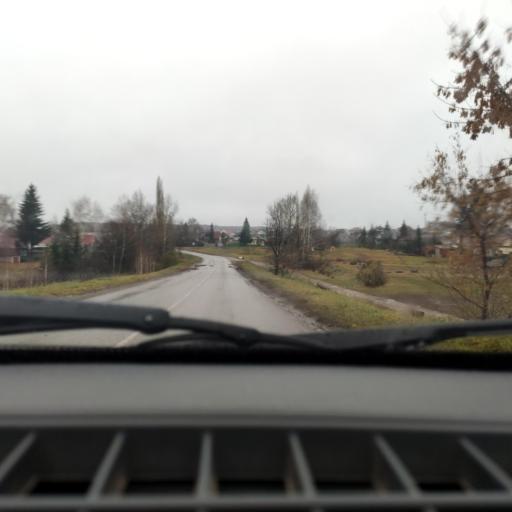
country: RU
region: Bashkortostan
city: Avdon
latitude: 54.6523
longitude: 55.7777
